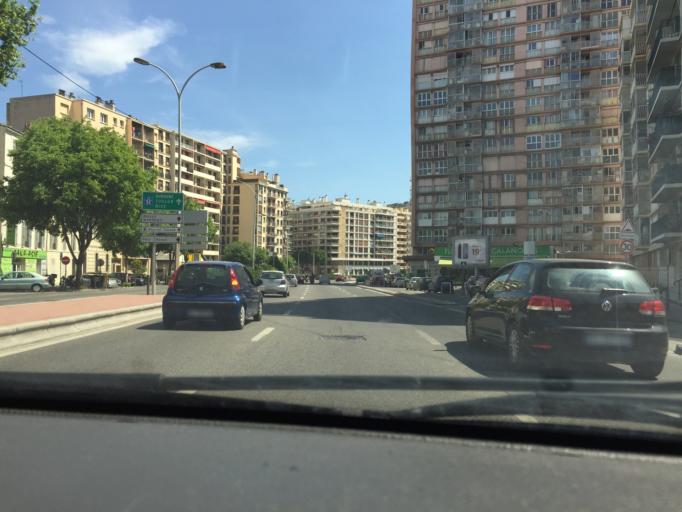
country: FR
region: Provence-Alpes-Cote d'Azur
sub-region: Departement des Bouches-du-Rhone
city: Marseille 05
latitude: 43.2953
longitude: 5.4005
